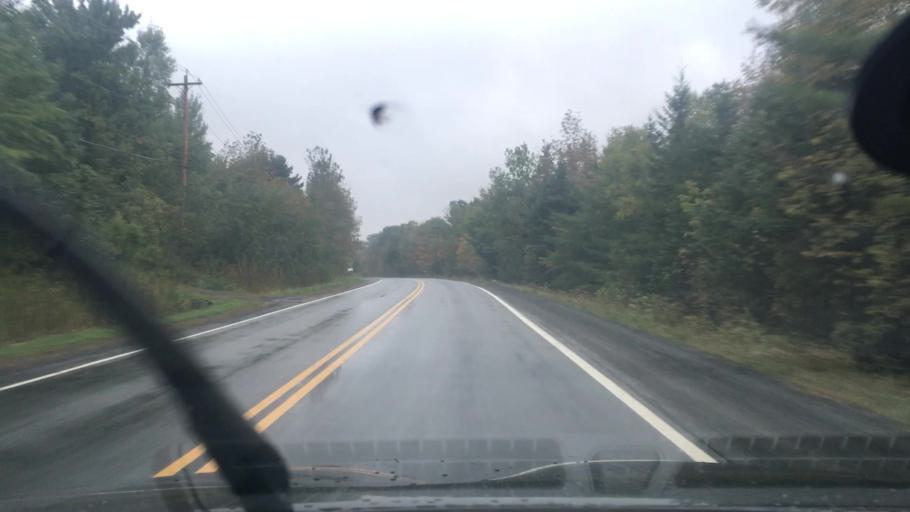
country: CA
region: Nova Scotia
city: Windsor
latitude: 44.8437
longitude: -64.2281
